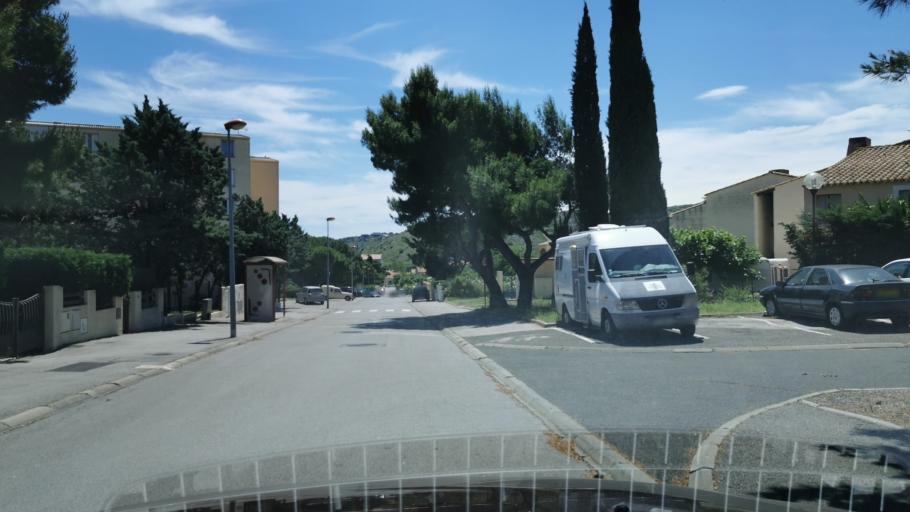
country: FR
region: Languedoc-Roussillon
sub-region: Departement de l'Aude
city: Narbonne
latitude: 43.1841
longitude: 2.9713
